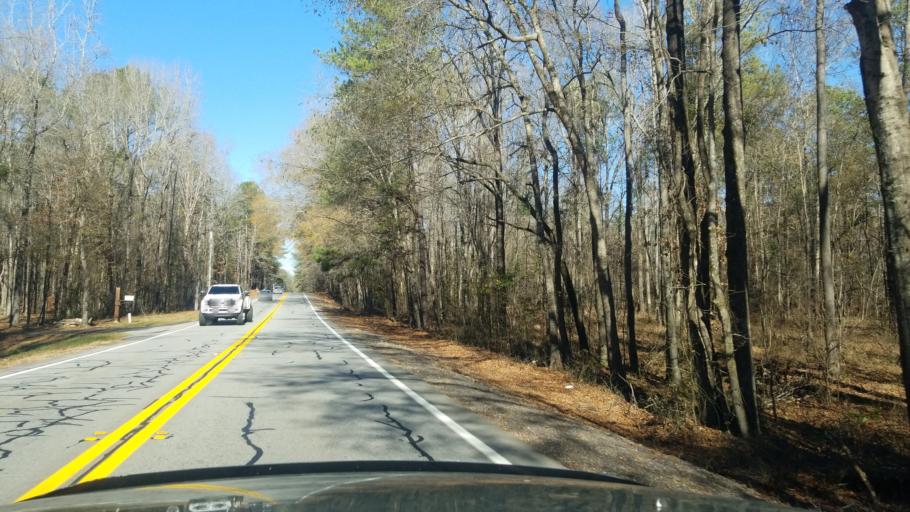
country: US
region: Georgia
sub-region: Harris County
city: Hamilton
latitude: 32.6671
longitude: -84.8587
